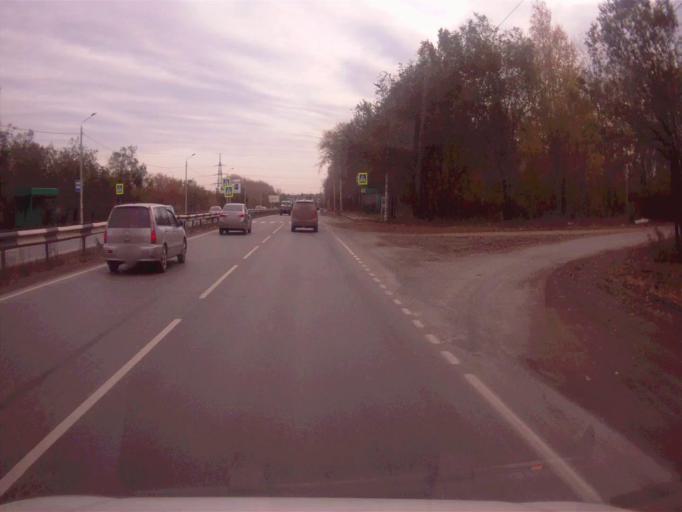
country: RU
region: Chelyabinsk
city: Novosineglazovskiy
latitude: 55.0523
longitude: 61.4110
